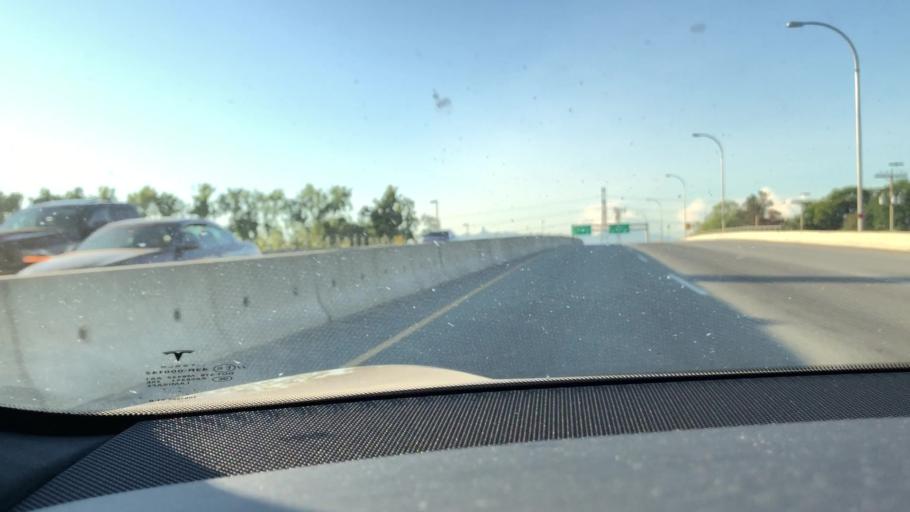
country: CA
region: British Columbia
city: Ladner
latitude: 49.0881
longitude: -123.0245
